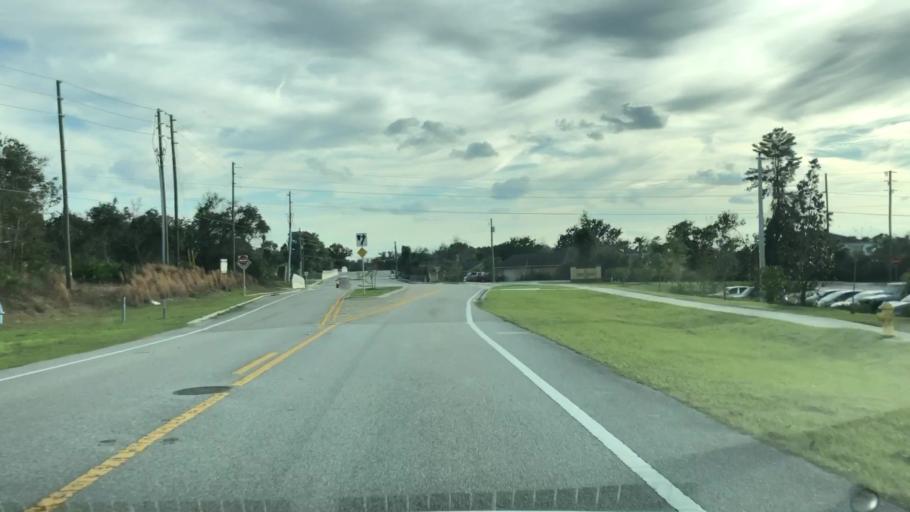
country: US
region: Florida
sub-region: Volusia County
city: Deltona
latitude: 28.9312
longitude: -81.2611
